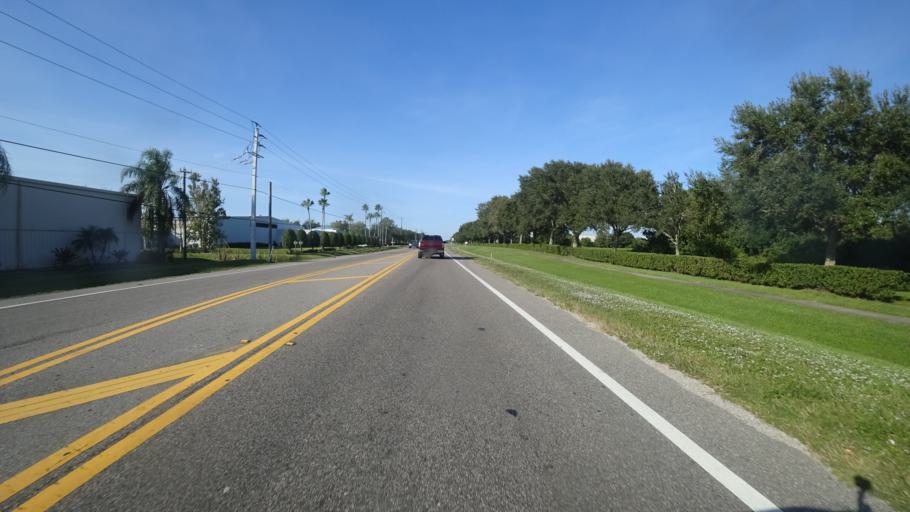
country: US
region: Florida
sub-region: Manatee County
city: Whitfield
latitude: 27.4087
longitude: -82.5467
